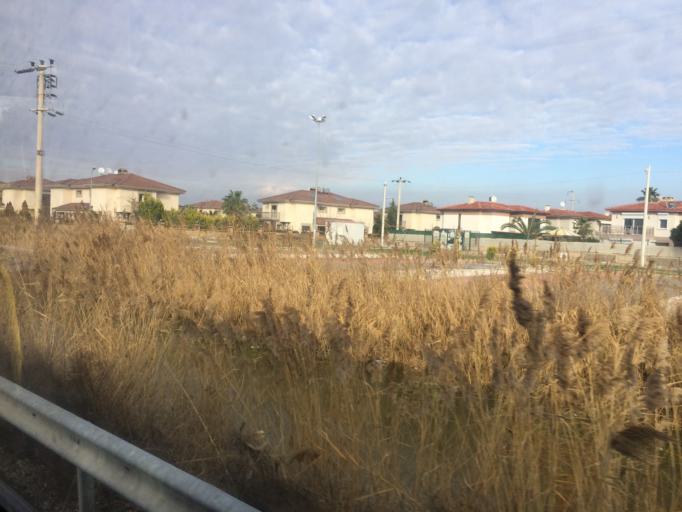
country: TR
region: Izmir
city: Menemen
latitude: 38.5019
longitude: 26.9598
